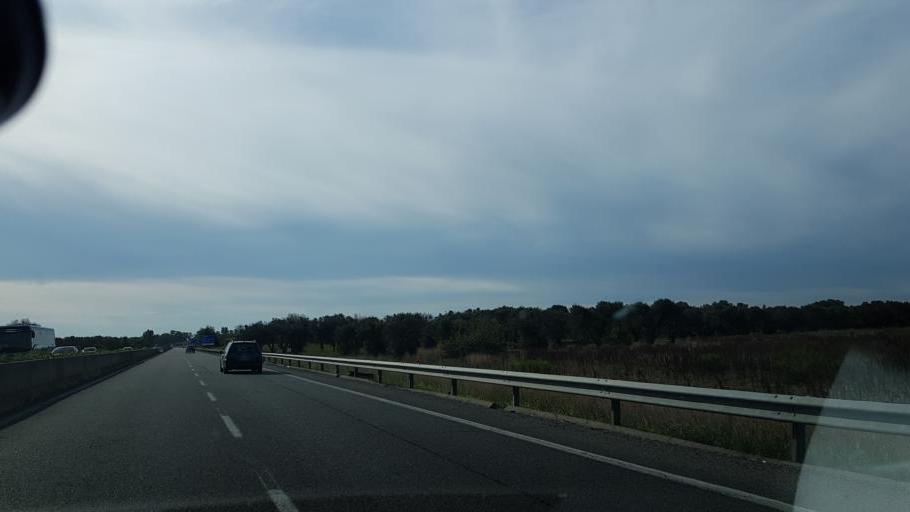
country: IT
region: Apulia
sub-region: Provincia di Brindisi
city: San Pietro Vernotico
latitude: 40.5296
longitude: 18.0113
